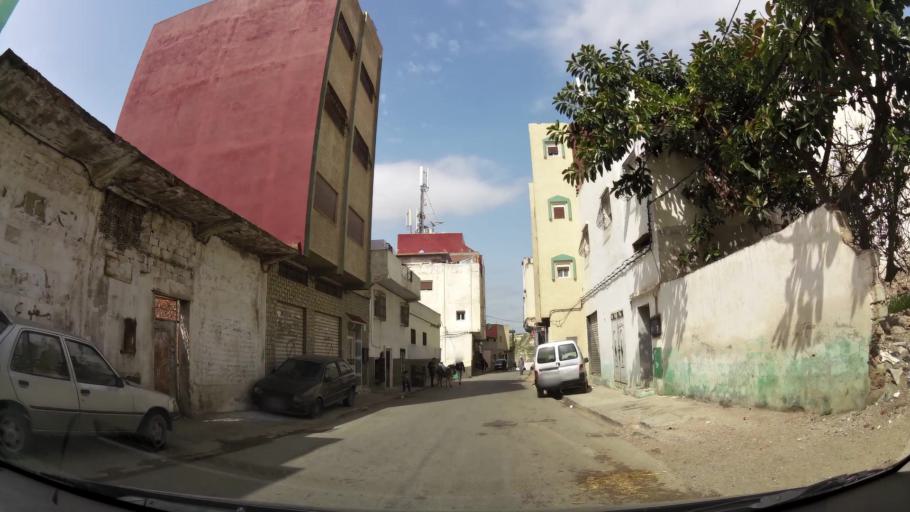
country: MA
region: Tanger-Tetouan
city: Tetouan
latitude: 35.5790
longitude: -5.3879
